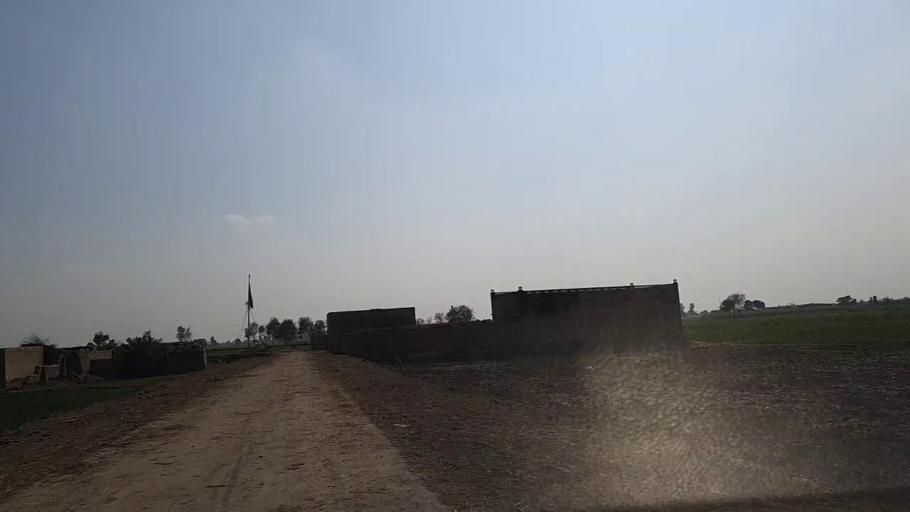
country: PK
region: Sindh
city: Jam Sahib
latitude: 26.3002
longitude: 68.5698
